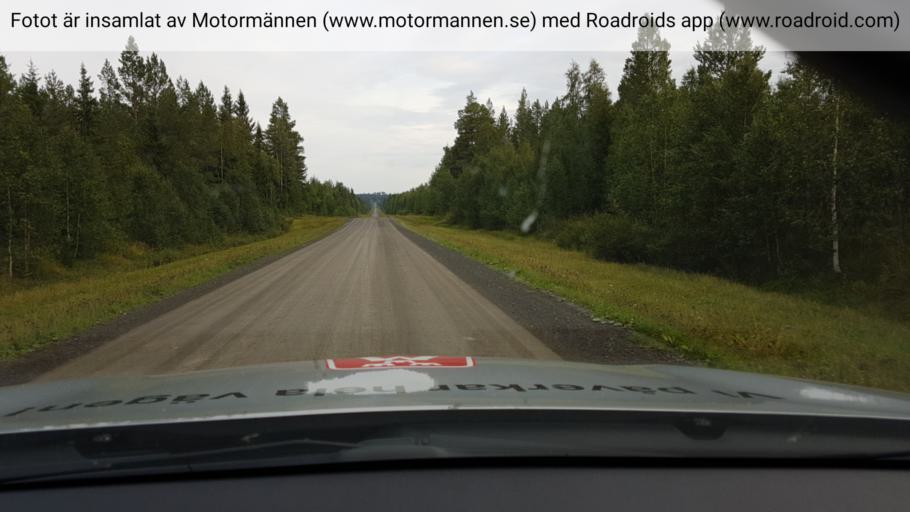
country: SE
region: Jaemtland
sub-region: OEstersunds Kommun
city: Lit
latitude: 63.6613
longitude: 14.9115
